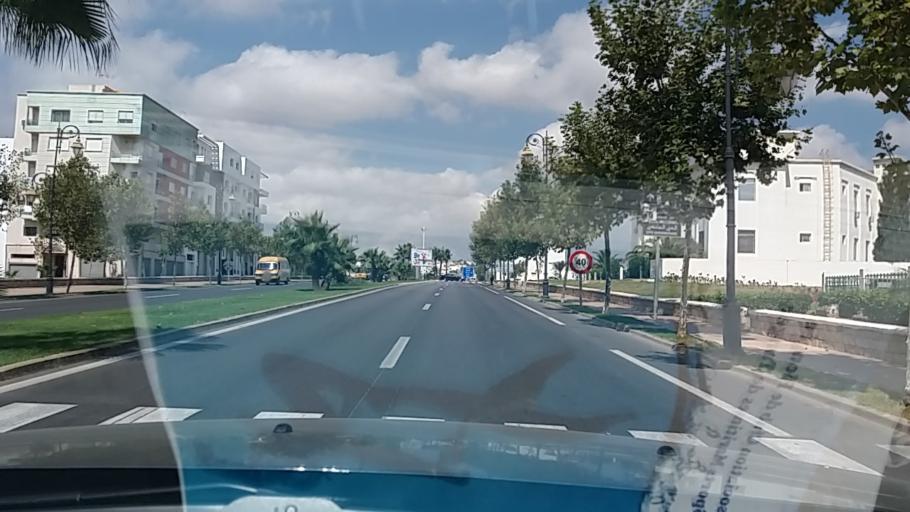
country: MA
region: Tanger-Tetouan
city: Tetouan
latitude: 35.5904
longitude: -5.3352
